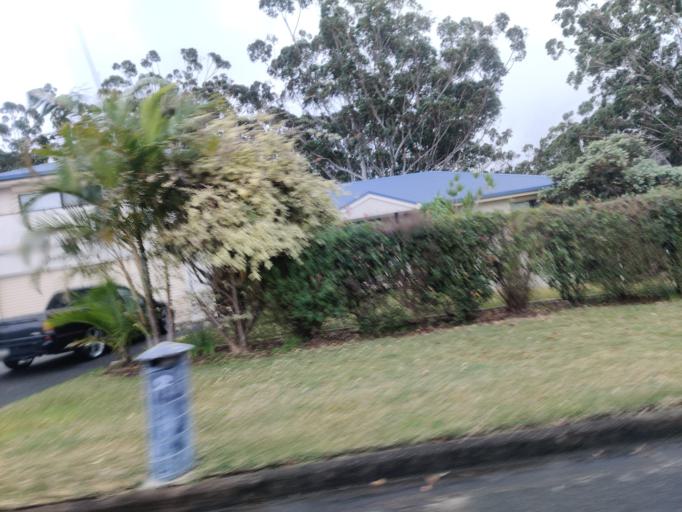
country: AU
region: New South Wales
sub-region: Great Lakes
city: Forster
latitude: -32.3762
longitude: 152.5036
